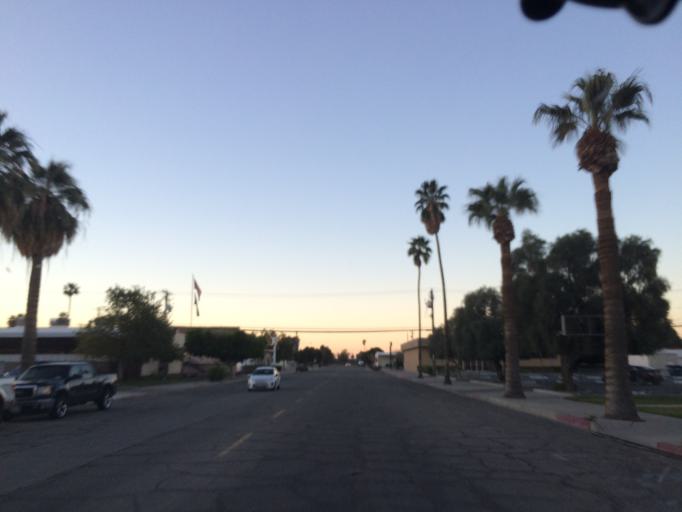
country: US
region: California
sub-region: Riverside County
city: Blythe
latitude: 33.6117
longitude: -114.5955
